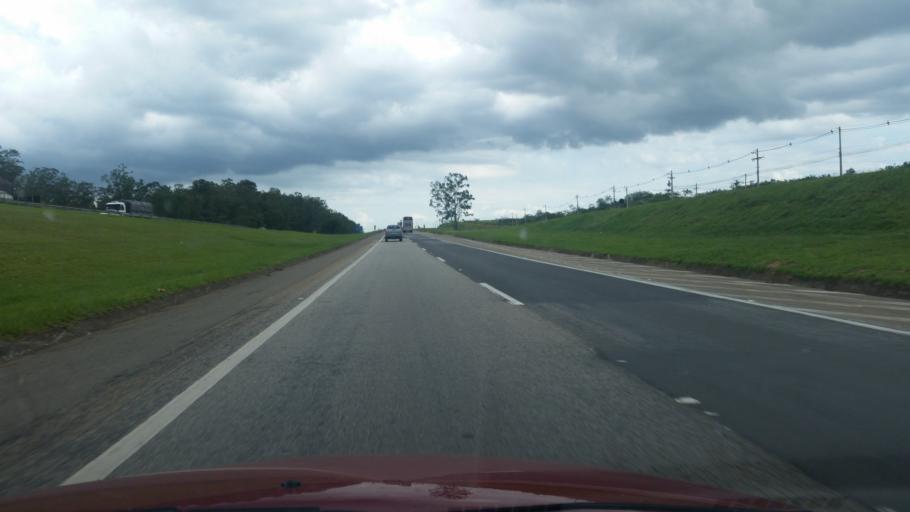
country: BR
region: Sao Paulo
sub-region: Sorocaba
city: Sorocaba
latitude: -23.3644
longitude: -47.4767
